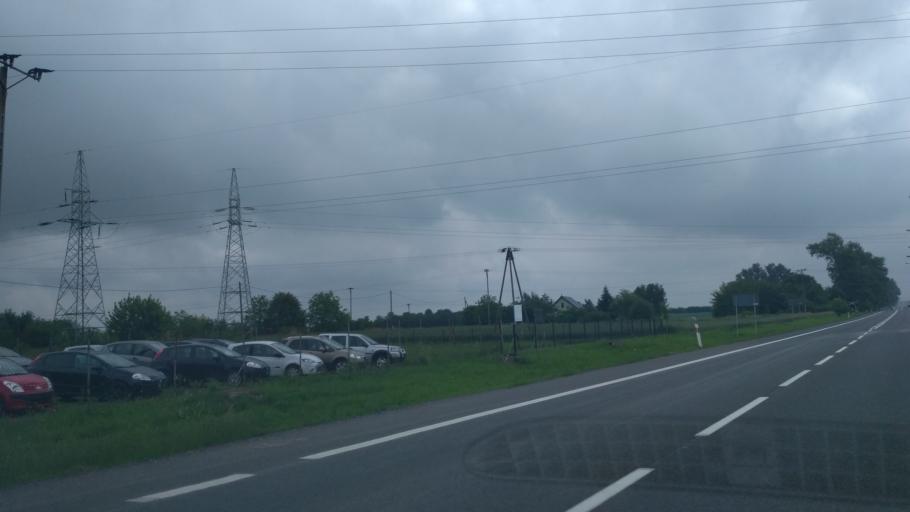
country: PL
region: Subcarpathian Voivodeship
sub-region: Powiat przeworski
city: Przeworsk
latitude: 50.0548
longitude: 22.5111
